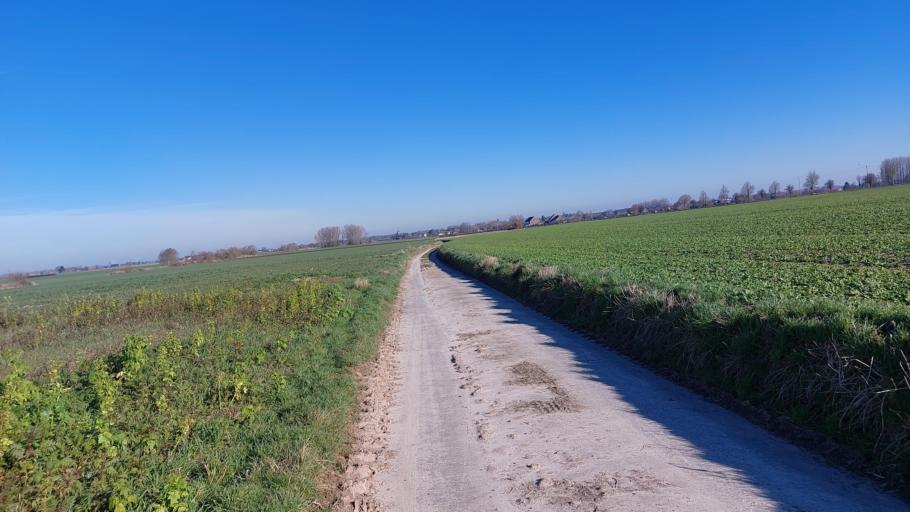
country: BE
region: Wallonia
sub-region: Province du Hainaut
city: Chievres
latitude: 50.5635
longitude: 3.8033
